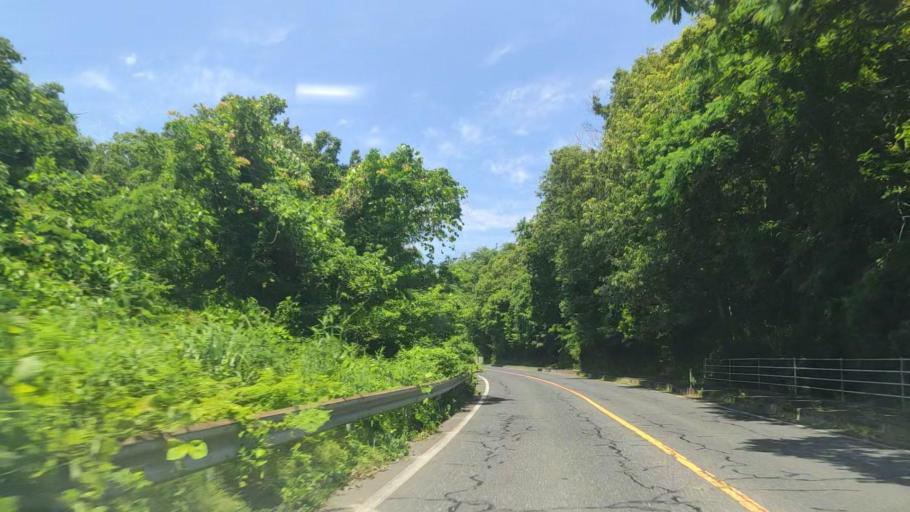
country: JP
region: Tottori
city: Tottori
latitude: 35.5274
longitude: 134.2301
